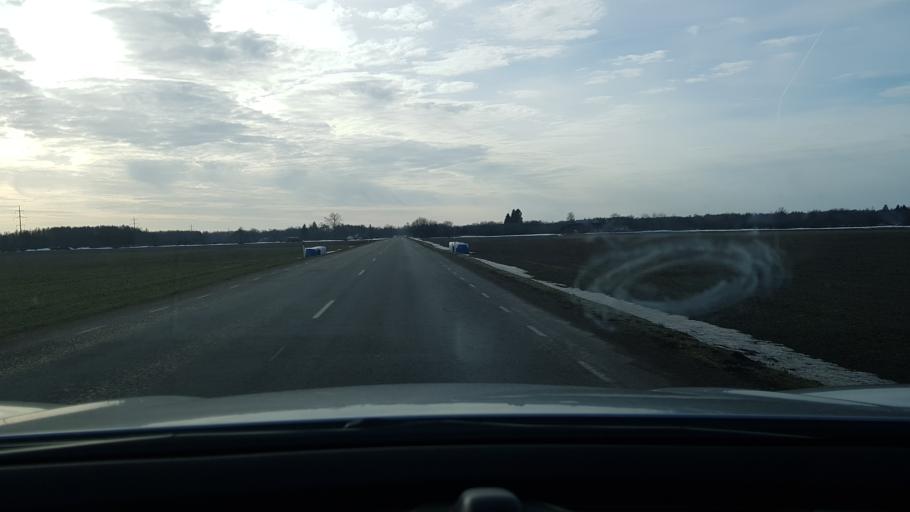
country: EE
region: Saare
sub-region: Kuressaare linn
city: Kuressaare
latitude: 58.3155
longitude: 22.5449
